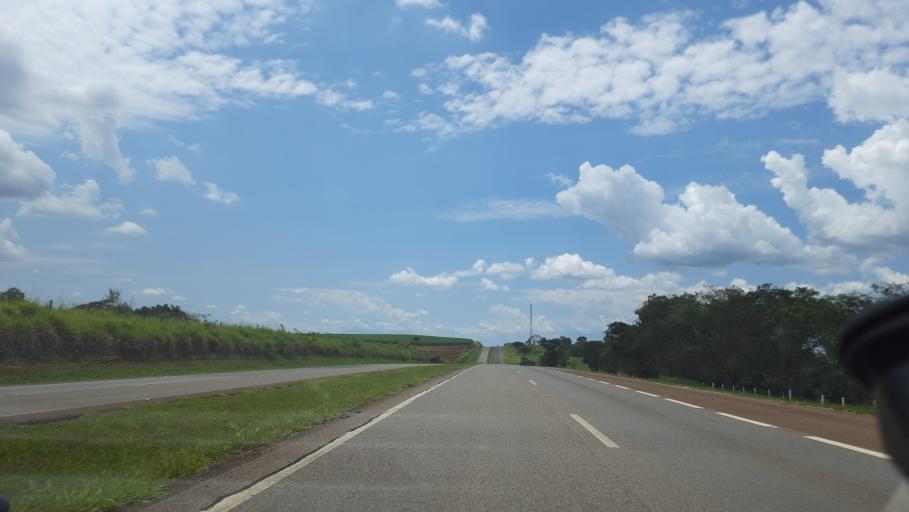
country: BR
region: Sao Paulo
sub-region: Casa Branca
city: Casa Branca
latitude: -21.6947
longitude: -47.0781
